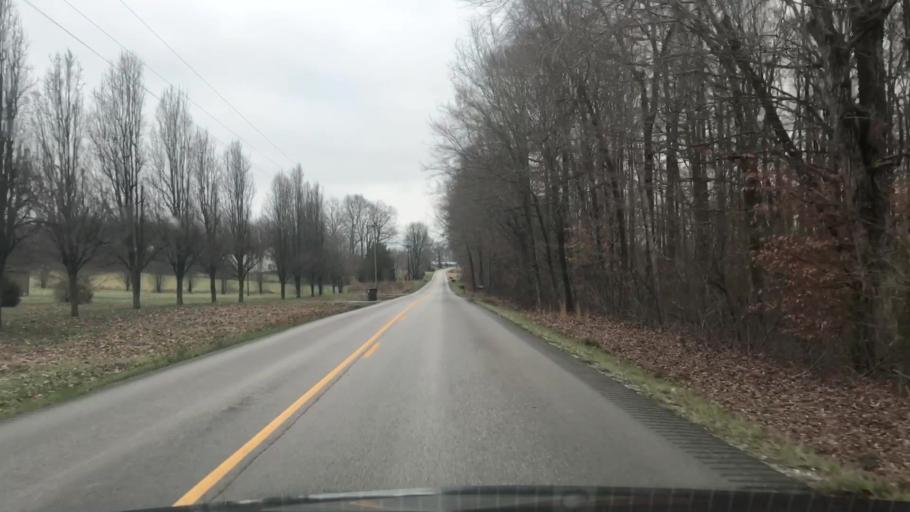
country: US
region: Kentucky
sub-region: Barren County
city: Glasgow
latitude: 36.8816
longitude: -85.7903
